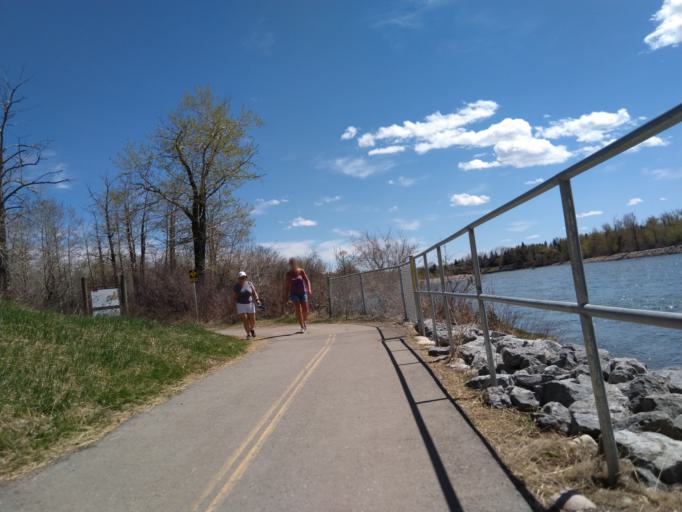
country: CA
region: Alberta
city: Calgary
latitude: 51.0992
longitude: -114.2101
